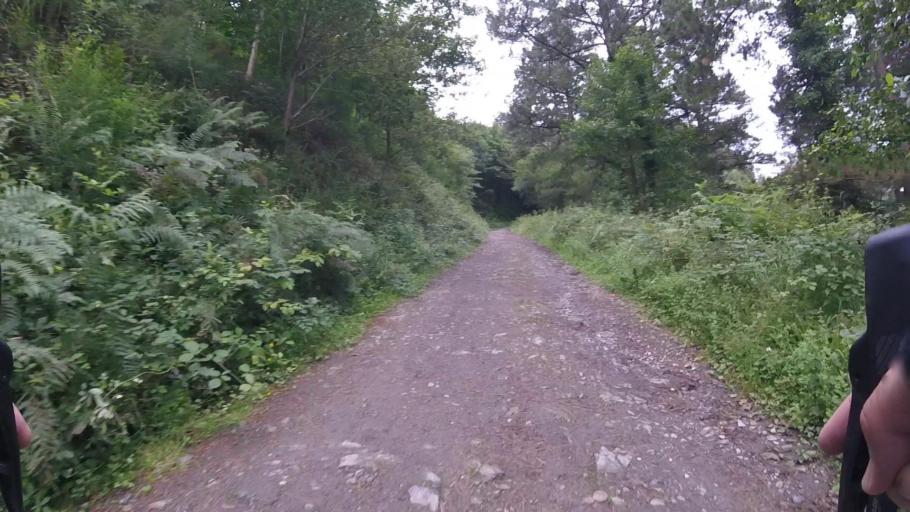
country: ES
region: Navarre
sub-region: Provincia de Navarra
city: Arano
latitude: 43.2540
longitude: -1.8892
